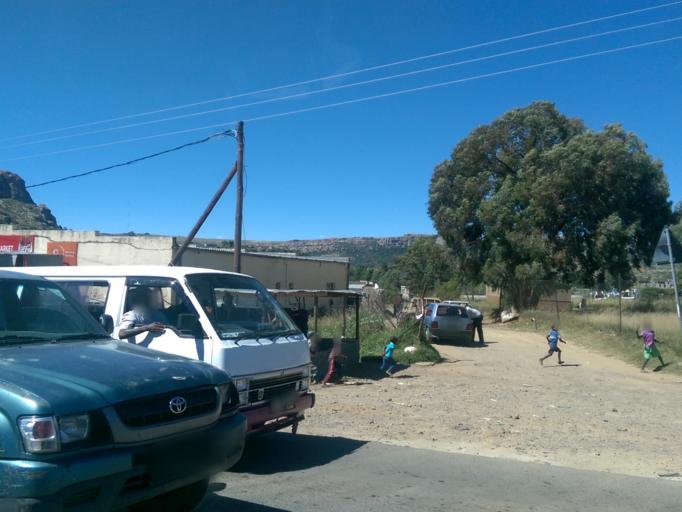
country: LS
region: Maseru
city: Maseru
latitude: -29.3635
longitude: 27.5304
